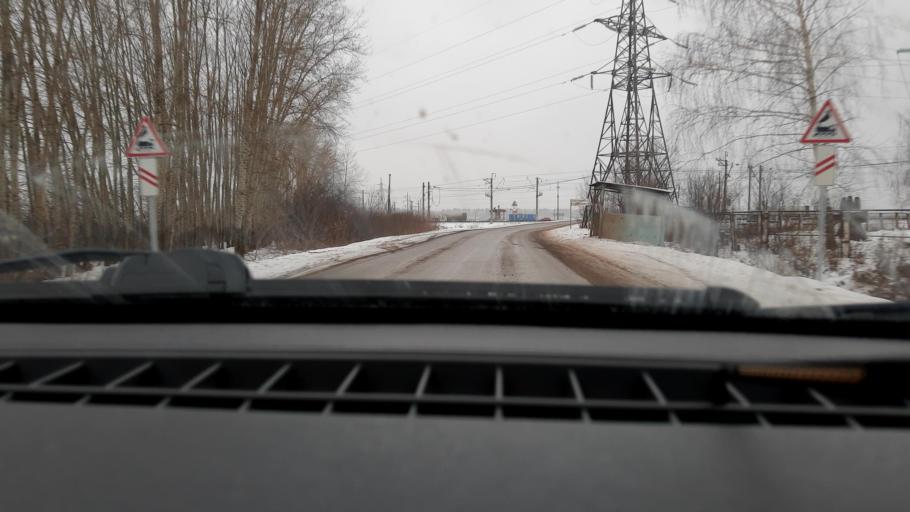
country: RU
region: Bashkortostan
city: Kabakovo
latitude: 54.7009
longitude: 56.2188
